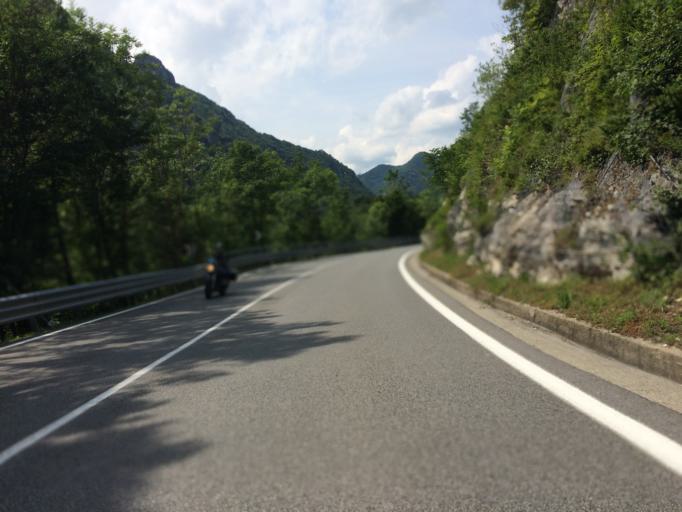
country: IT
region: Piedmont
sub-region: Provincia di Cuneo
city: Vernante
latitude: 44.2318
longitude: 7.5529
